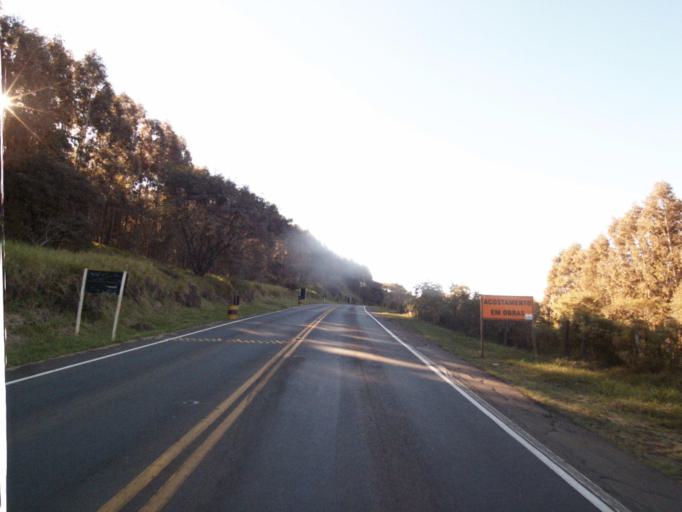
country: AR
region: Misiones
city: Bernardo de Irigoyen
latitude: -26.4741
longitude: -53.5073
